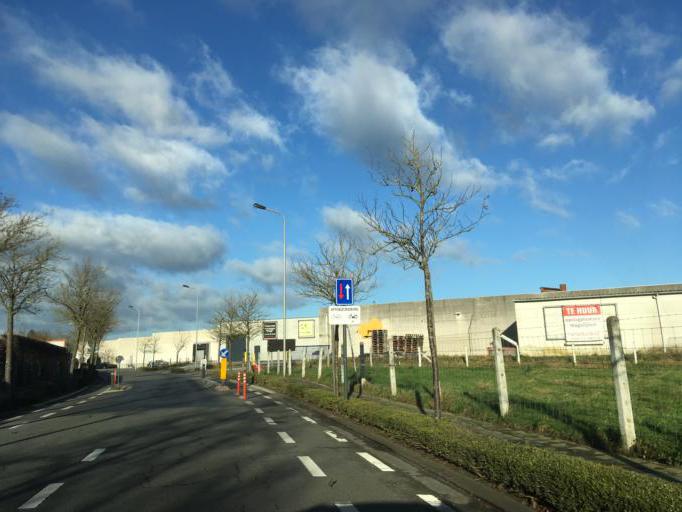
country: BE
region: Flanders
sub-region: Provincie West-Vlaanderen
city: Ingelmunster
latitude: 50.9277
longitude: 3.2514
